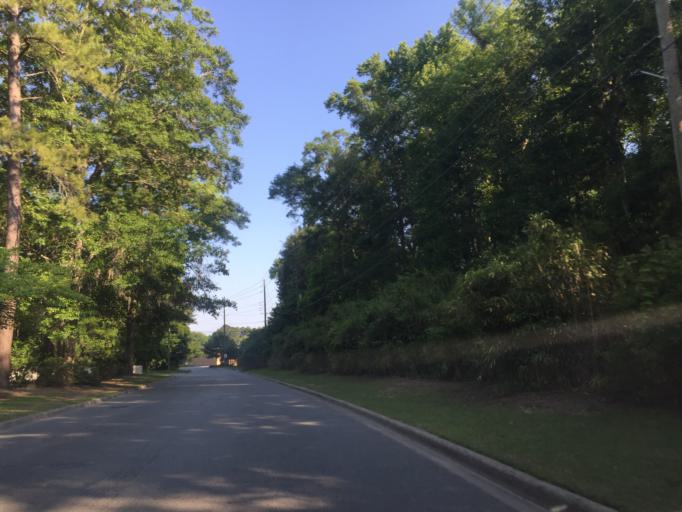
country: US
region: Georgia
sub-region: Chatham County
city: Isle of Hope
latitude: 31.9895
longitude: -81.0757
